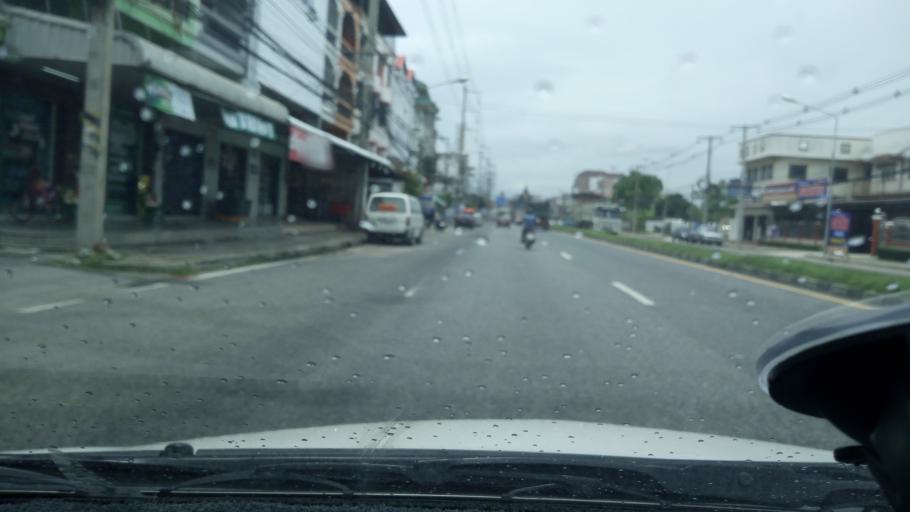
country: TH
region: Chon Buri
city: Phanat Nikhom
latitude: 13.4494
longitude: 101.1731
